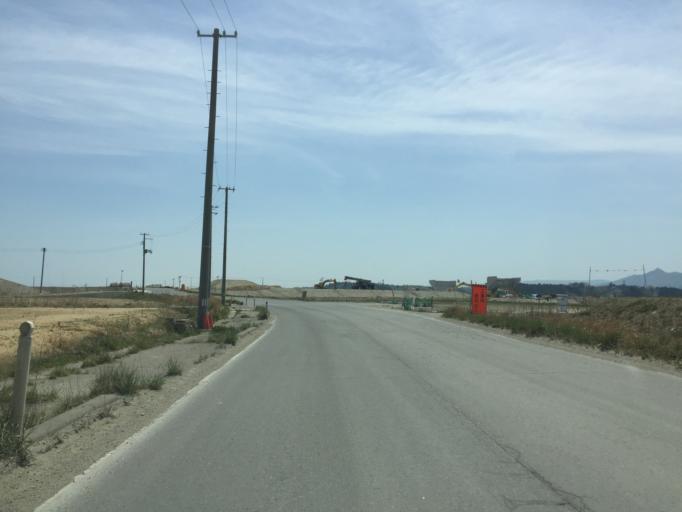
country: JP
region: Miyagi
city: Watari
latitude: 37.9348
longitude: 140.9122
